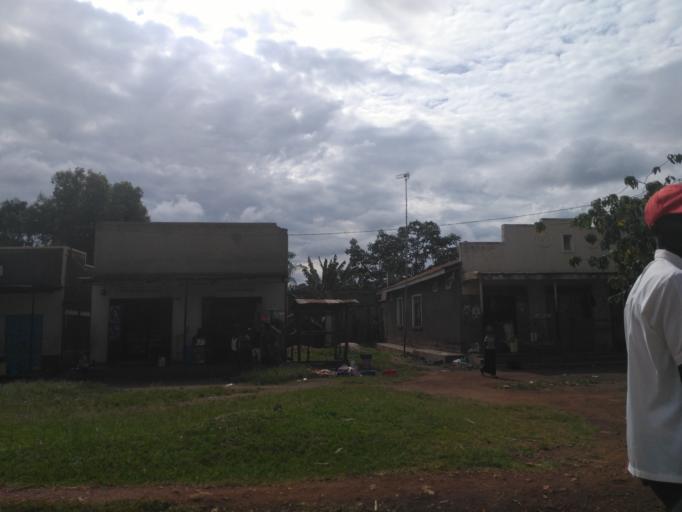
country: UG
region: Central Region
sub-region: Buikwe District
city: Njeru
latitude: 0.3932
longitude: 33.1712
